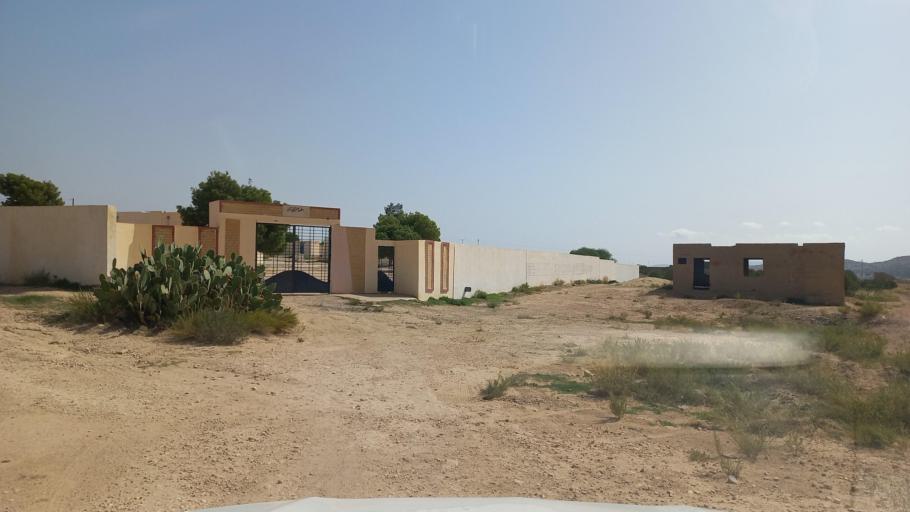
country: TN
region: Al Qasrayn
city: Sbiba
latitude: 35.3934
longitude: 8.9549
